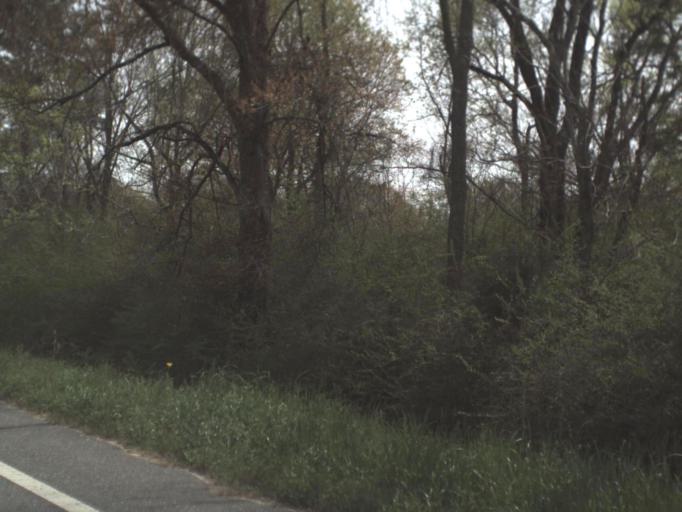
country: US
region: Florida
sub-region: Jackson County
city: Graceville
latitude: 30.9473
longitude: -85.3914
